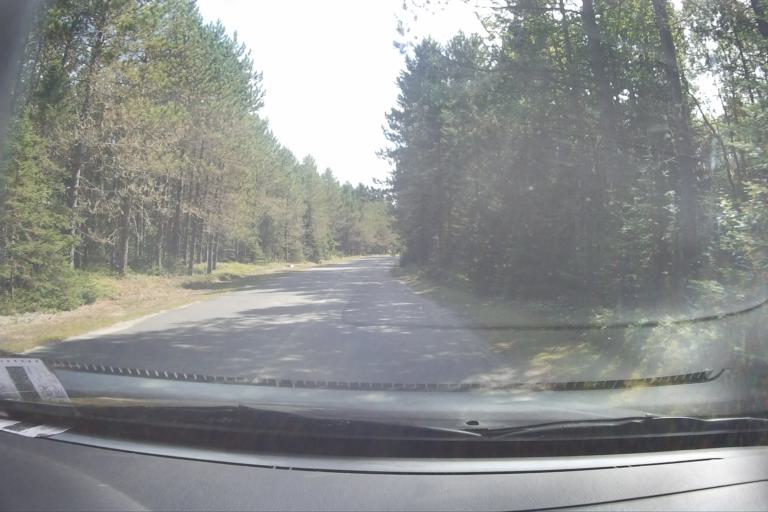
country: CA
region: Ontario
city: Marathon
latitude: 48.7881
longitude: -86.6234
